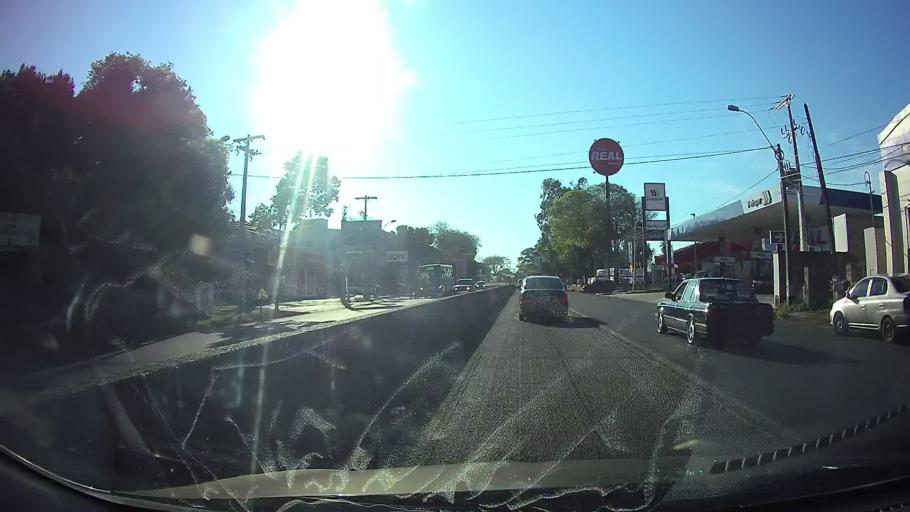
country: PY
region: Central
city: Capiata
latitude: -25.3515
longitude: -57.4467
